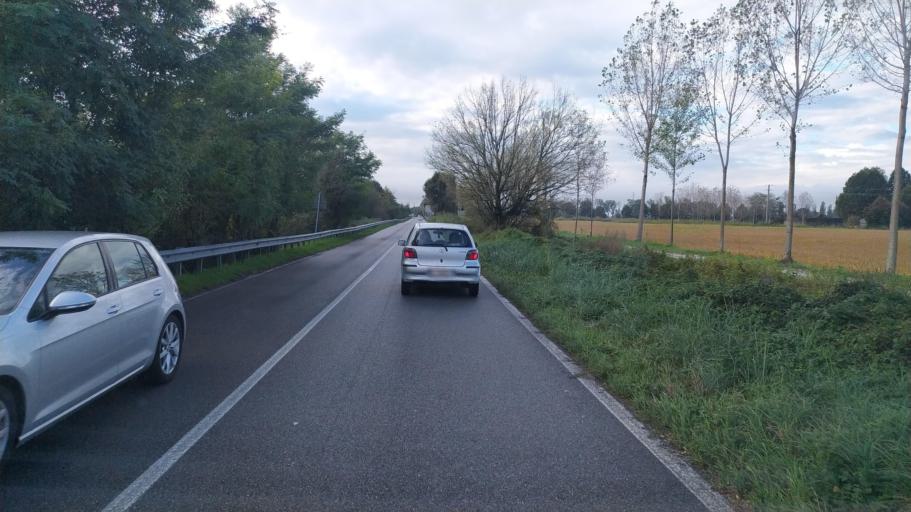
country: IT
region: Lombardy
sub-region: Citta metropolitana di Milano
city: Gaggiano
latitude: 45.3939
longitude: 9.0295
